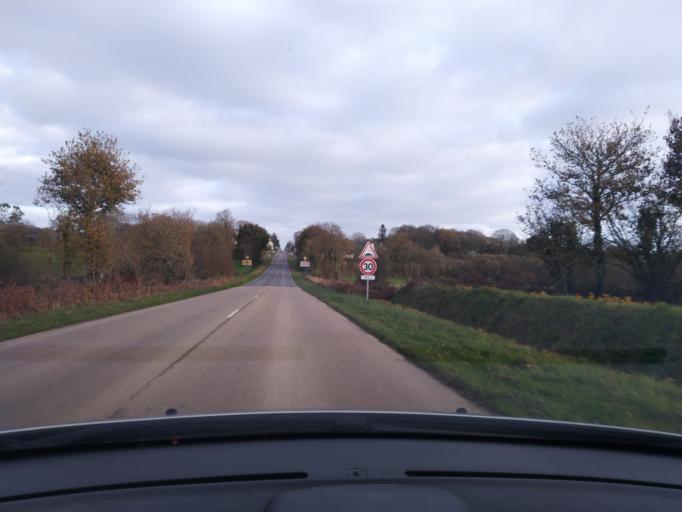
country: FR
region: Brittany
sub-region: Departement du Finistere
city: Plourin-les-Morlaix
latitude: 48.5763
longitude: -3.7720
